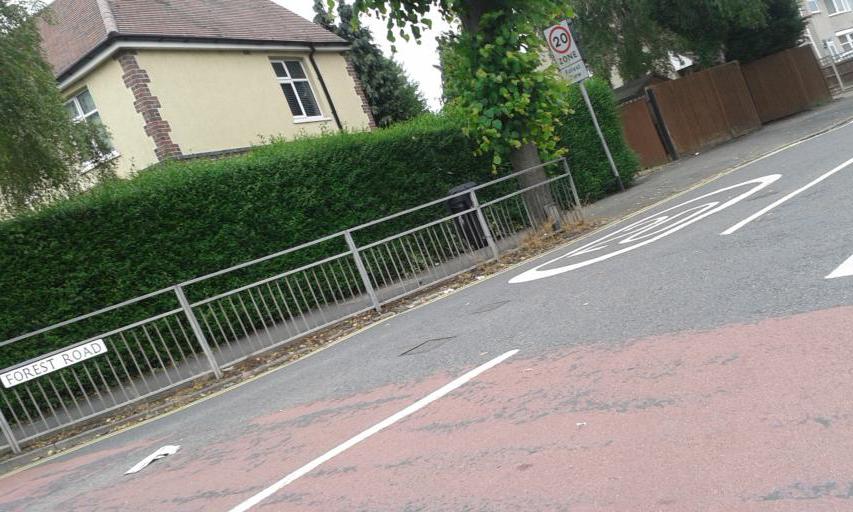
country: GB
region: England
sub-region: Leicestershire
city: Hinckley
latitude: 52.5401
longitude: -1.3572
